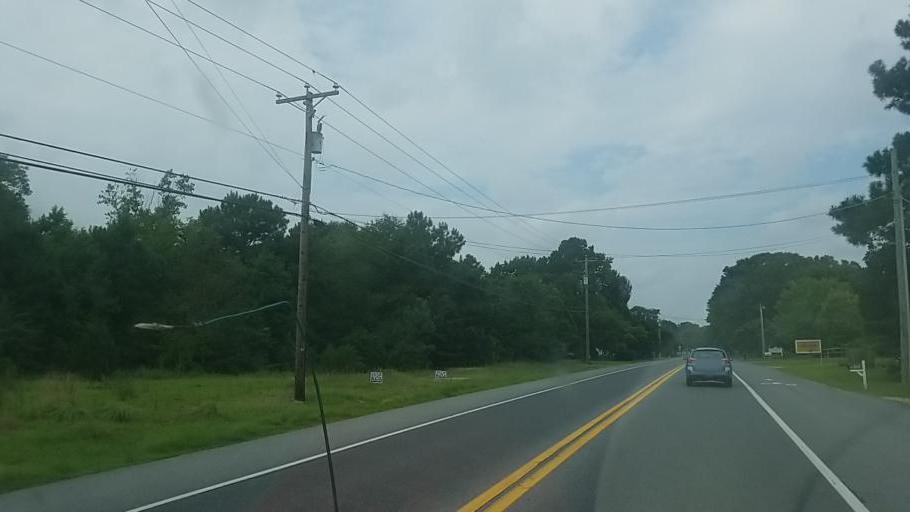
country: US
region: Delaware
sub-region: Sussex County
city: Ocean View
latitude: 38.5516
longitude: -75.1504
